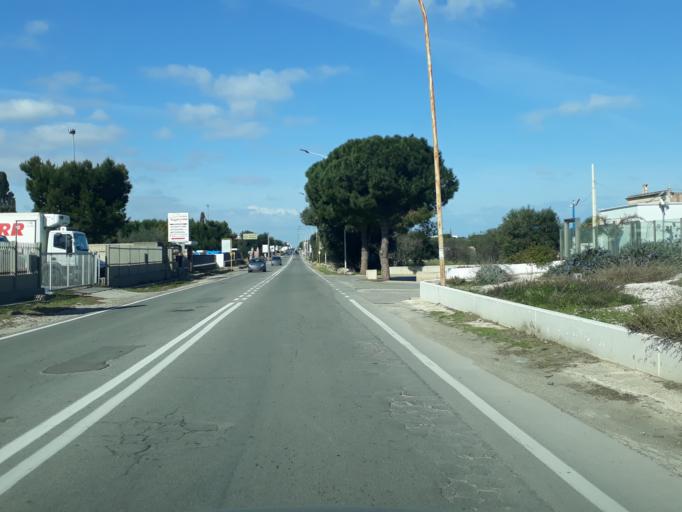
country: IT
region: Apulia
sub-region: Provincia di Bari
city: Monopoli
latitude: 40.9651
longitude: 17.2752
